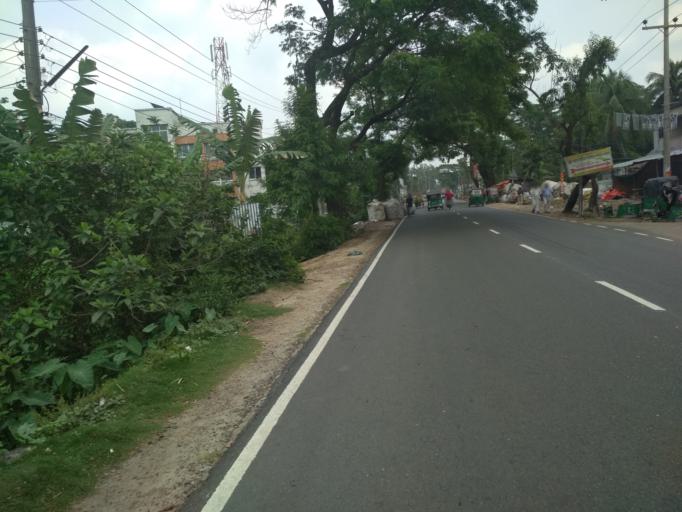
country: BD
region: Chittagong
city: Lakshmipur
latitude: 22.9421
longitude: 90.8460
